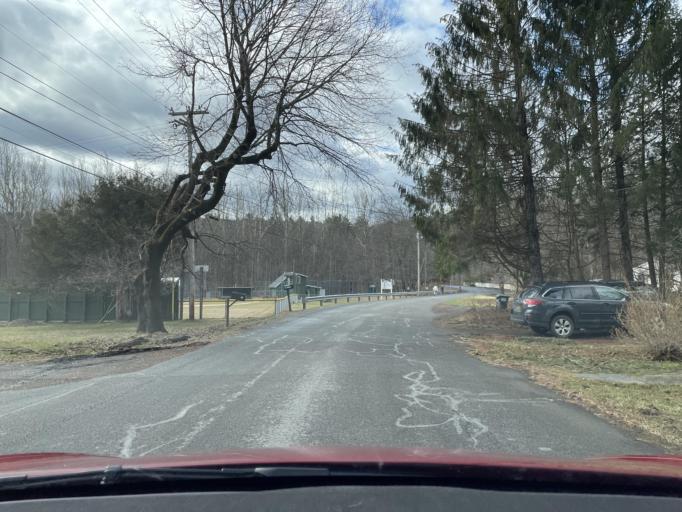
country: US
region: New York
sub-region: Ulster County
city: Woodstock
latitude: 42.0370
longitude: -74.1468
